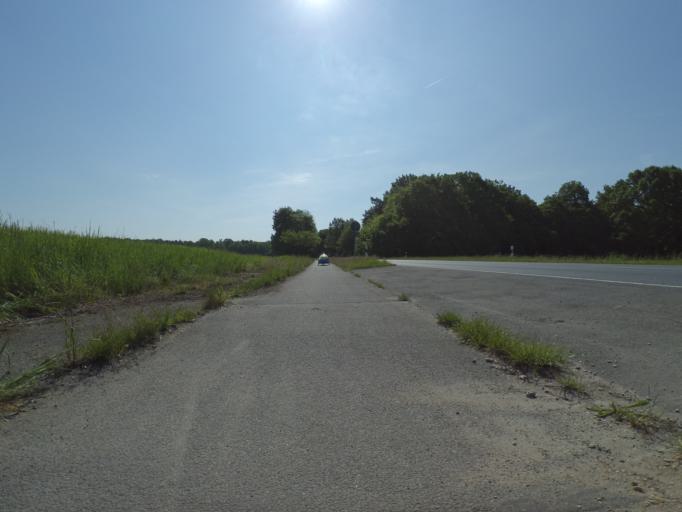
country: DE
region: Lower Saxony
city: Burgdorf
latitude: 52.4413
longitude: 9.9473
